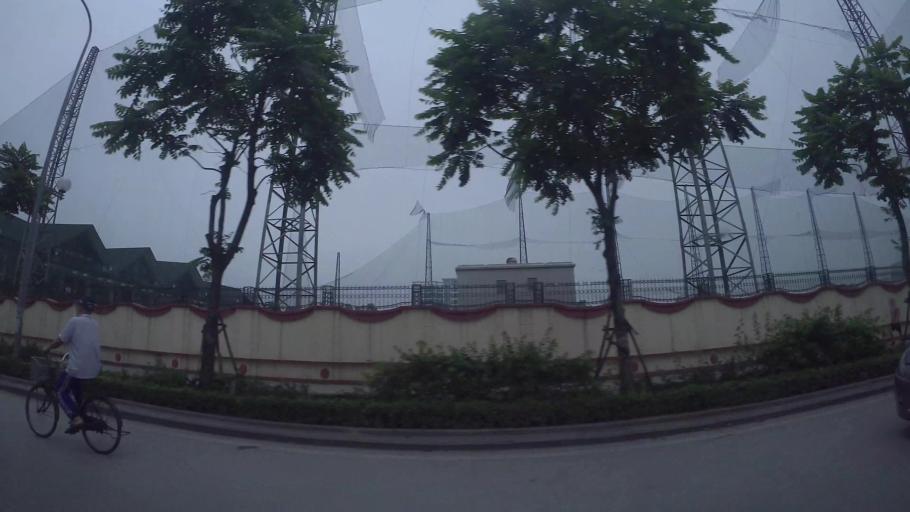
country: VN
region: Ha Noi
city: Hai BaTrung
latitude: 20.9911
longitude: 105.8334
